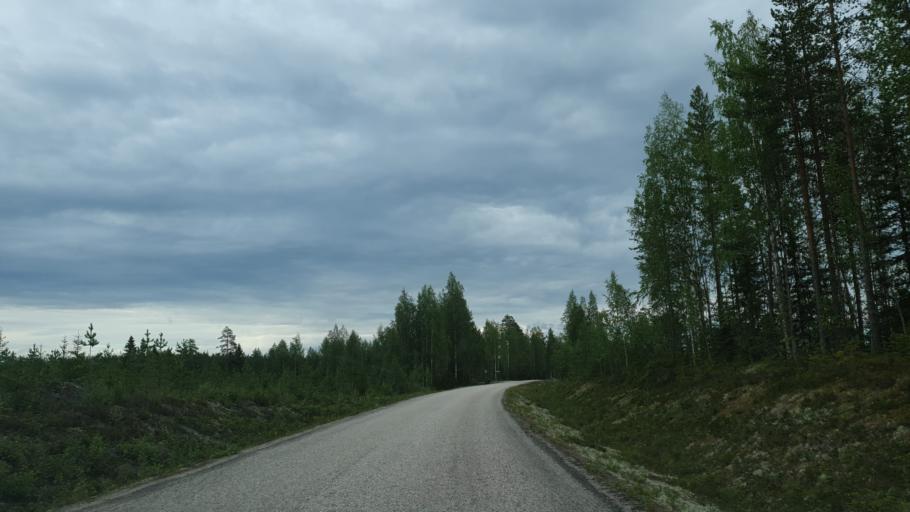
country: FI
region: Kainuu
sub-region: Kehys-Kainuu
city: Kuhmo
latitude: 64.3399
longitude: 29.3757
